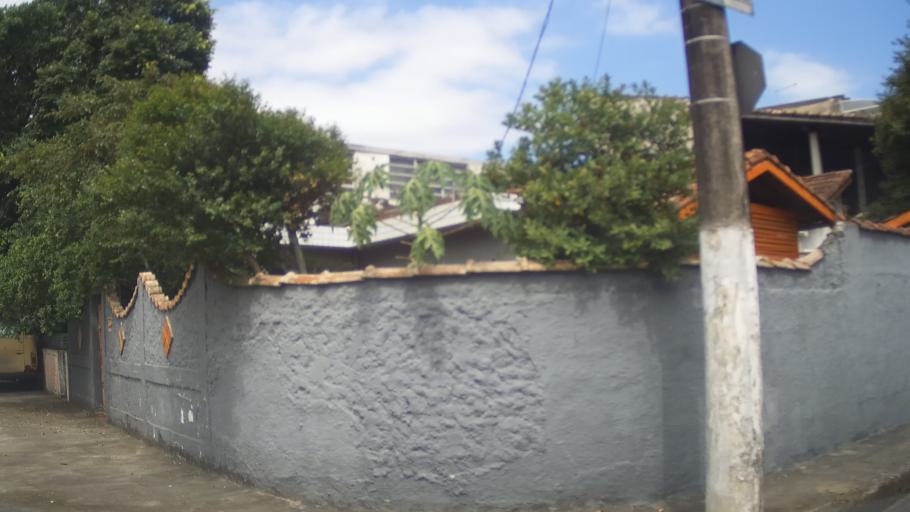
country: BR
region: Sao Paulo
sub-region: Santos
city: Santos
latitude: -23.9654
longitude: -46.3072
